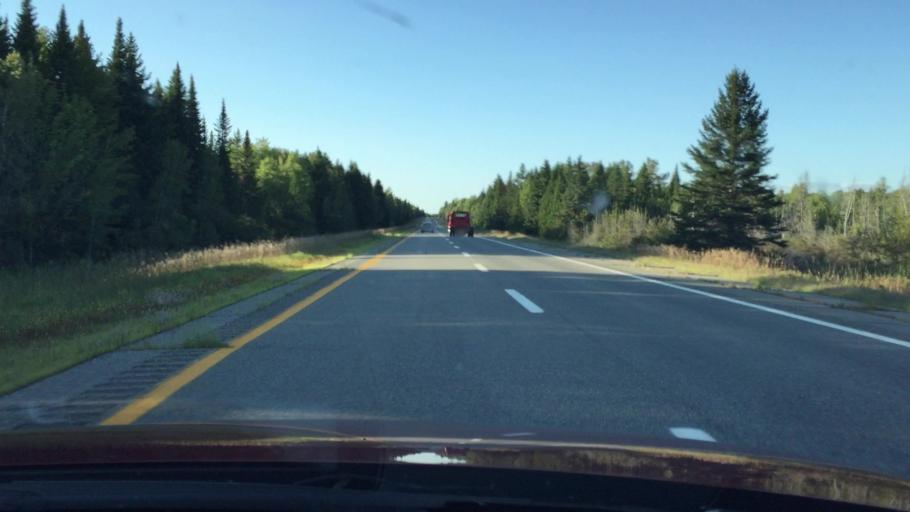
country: US
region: Maine
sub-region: Penobscot County
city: Patten
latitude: 45.8218
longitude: -68.4305
